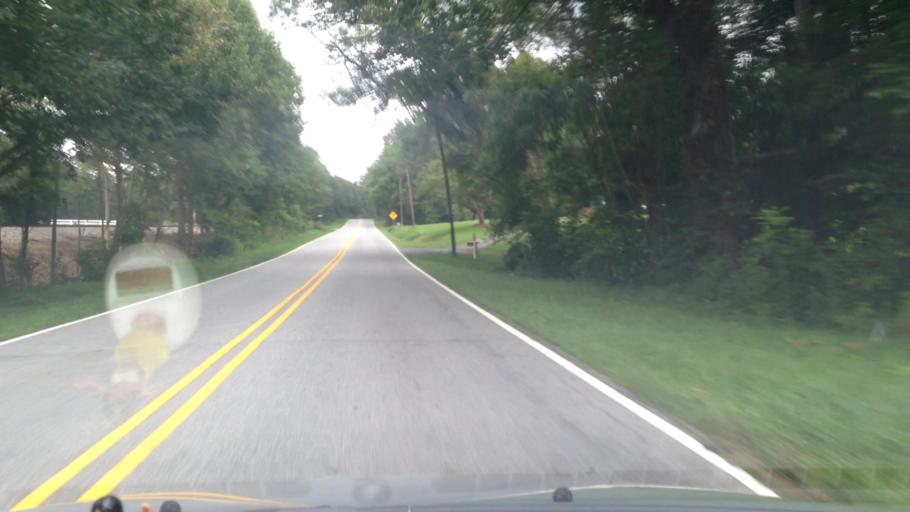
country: US
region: North Carolina
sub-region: Forsyth County
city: Walkertown
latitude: 36.2053
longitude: -80.1686
